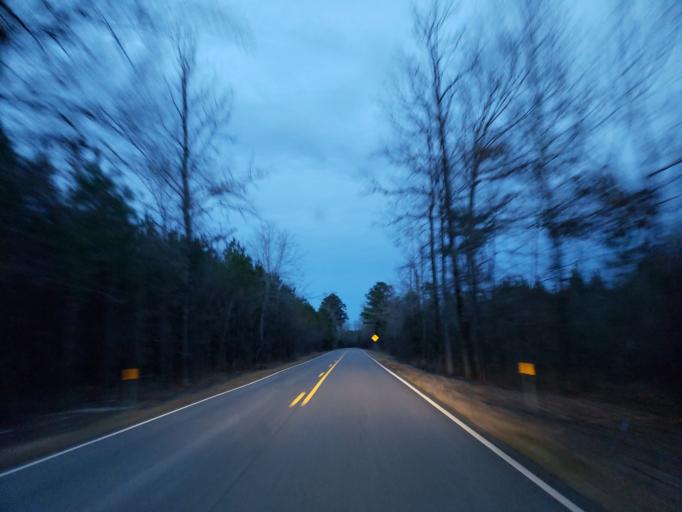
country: US
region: Alabama
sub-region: Greene County
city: Eutaw
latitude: 32.8868
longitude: -88.0488
